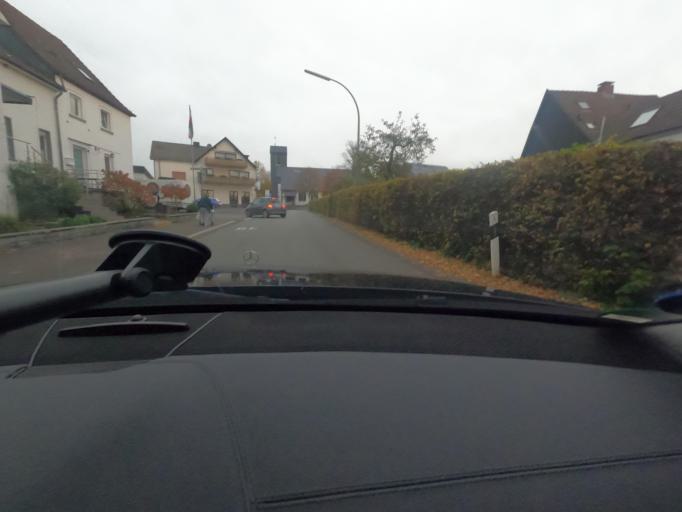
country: DE
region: North Rhine-Westphalia
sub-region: Regierungsbezirk Arnsberg
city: Mohnesee
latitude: 51.4806
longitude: 8.2000
